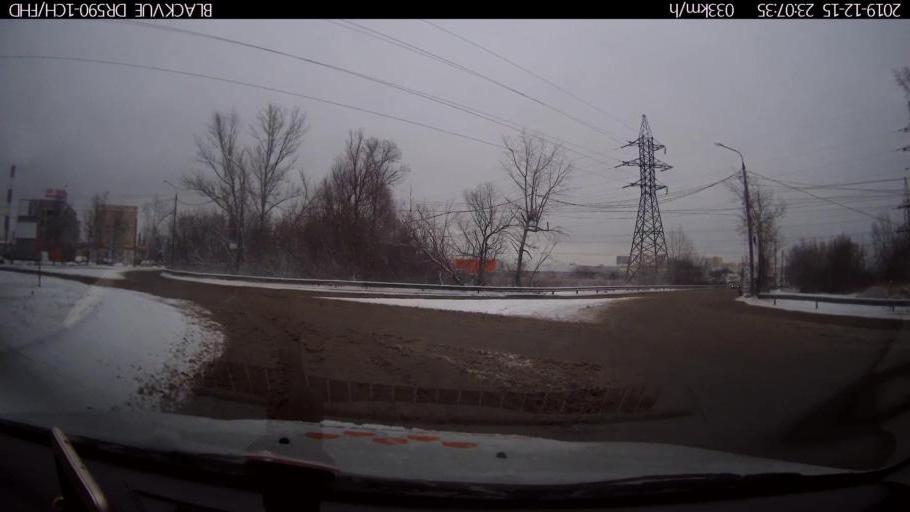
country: RU
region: Nizjnij Novgorod
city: Neklyudovo
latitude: 56.3451
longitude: 43.8885
